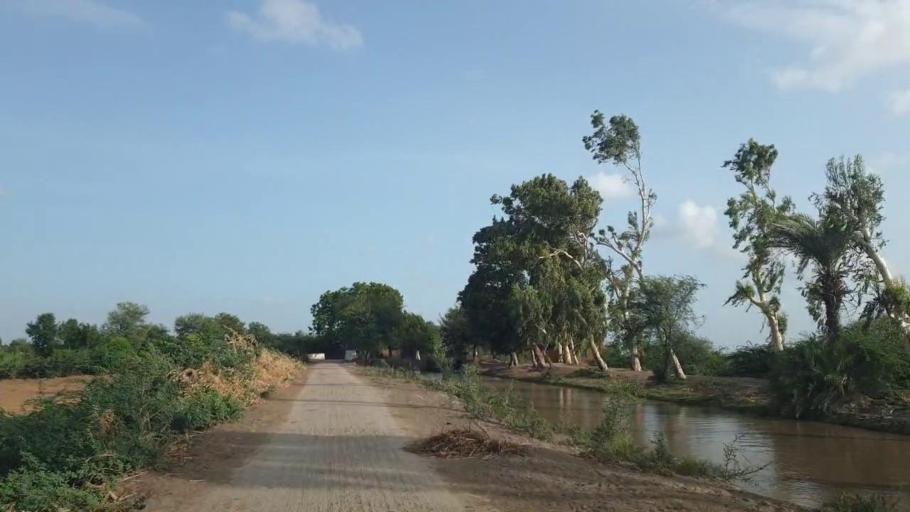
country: PK
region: Sindh
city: Kadhan
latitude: 24.6400
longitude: 69.1037
